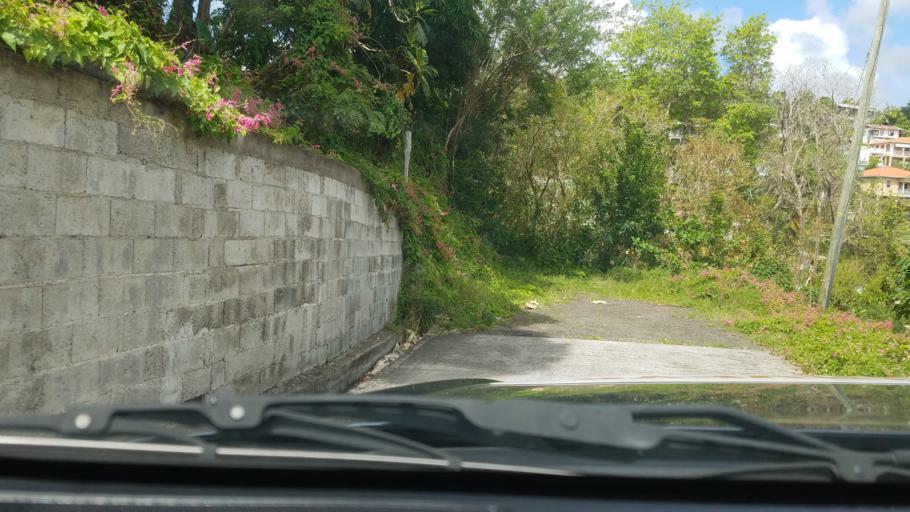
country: LC
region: Castries Quarter
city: Bisee
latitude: 14.0129
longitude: -60.9813
